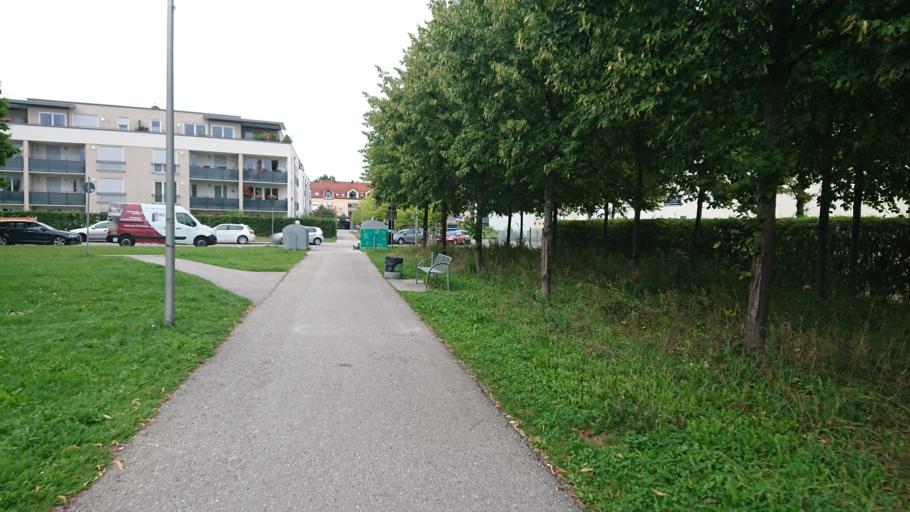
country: DE
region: Bavaria
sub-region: Swabia
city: Stadtbergen
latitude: 48.3674
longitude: 10.8696
